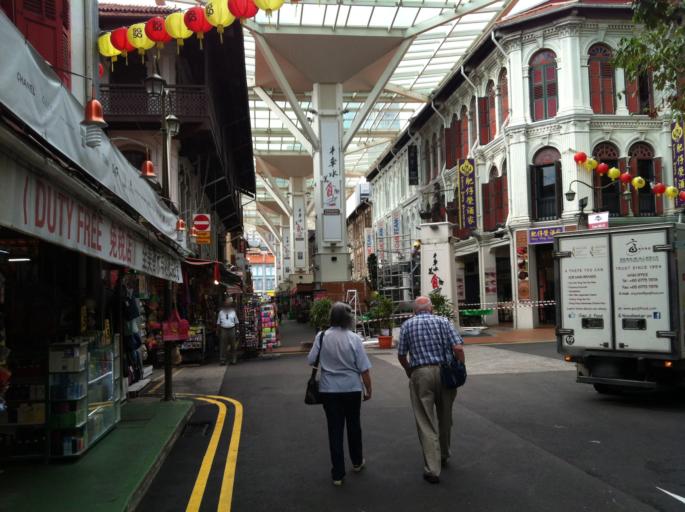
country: SG
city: Singapore
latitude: 1.2825
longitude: 103.8437
